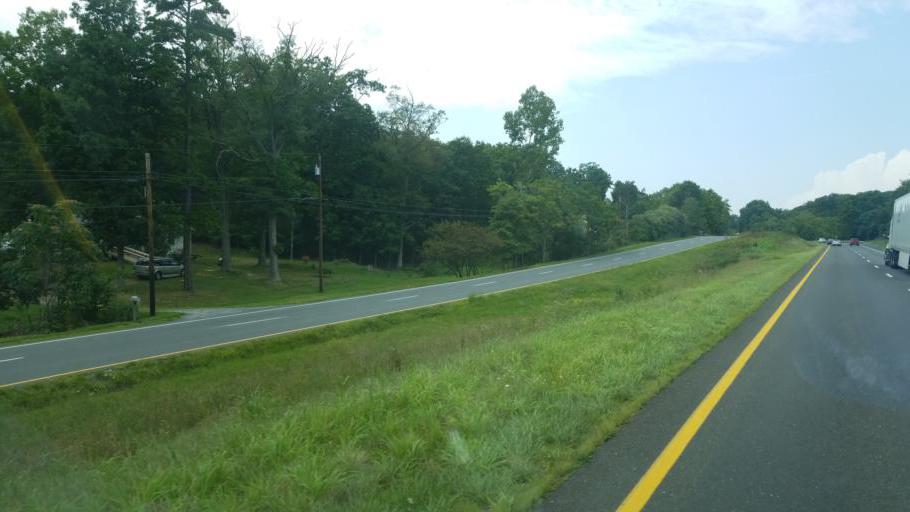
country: US
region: Virginia
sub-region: City of Winchester
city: Winchester
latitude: 39.2584
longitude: -78.2194
